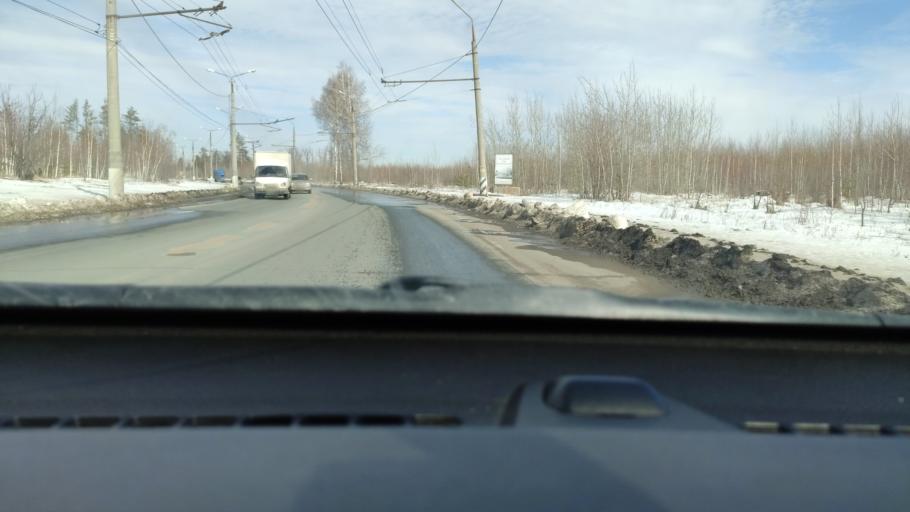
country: RU
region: Samara
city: Tol'yatti
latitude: 53.4802
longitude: 49.3700
